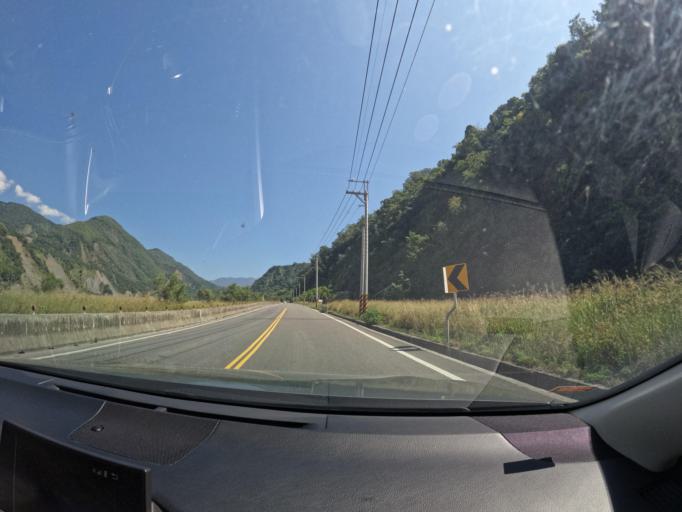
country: TW
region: Taiwan
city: Yujing
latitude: 23.1738
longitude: 120.7770
